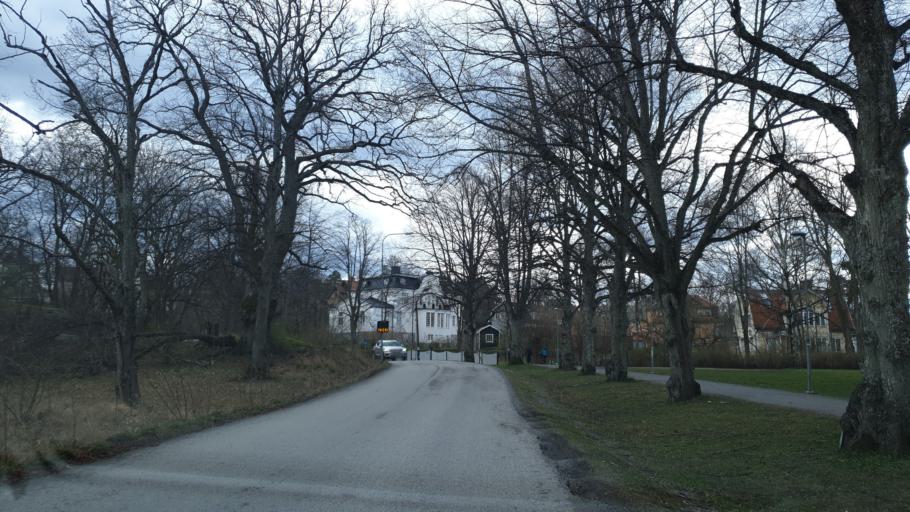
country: SE
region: Stockholm
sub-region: Nacka Kommun
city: Saltsjobaden
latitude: 59.2819
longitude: 18.3020
